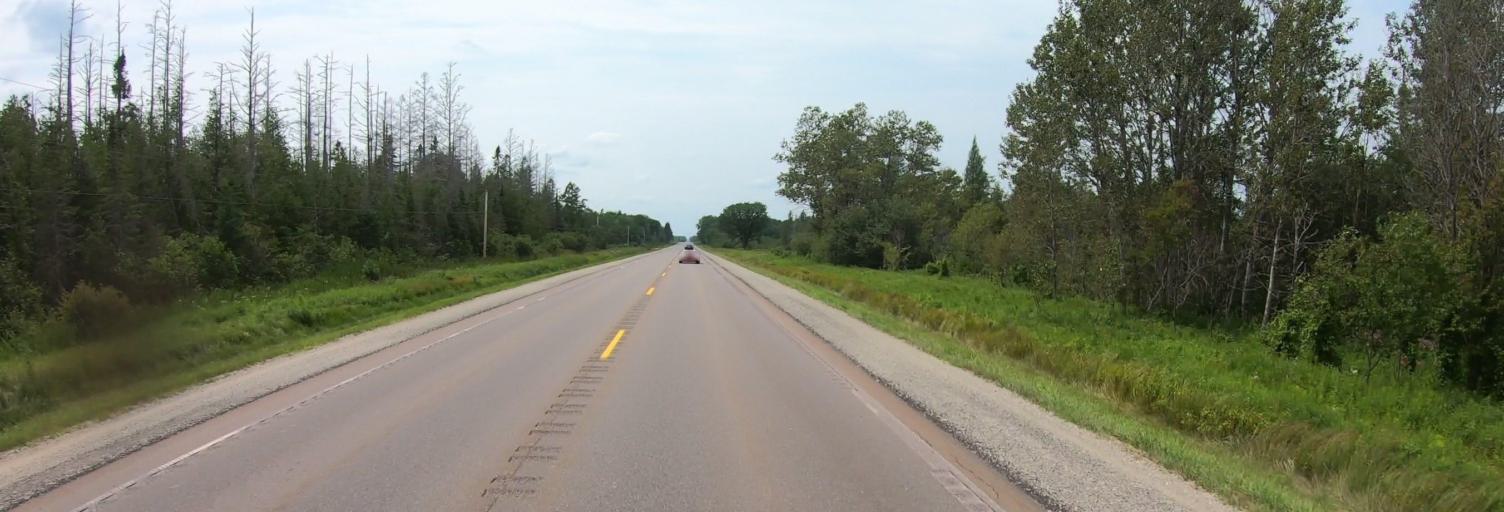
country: US
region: Michigan
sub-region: Marquette County
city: K. I. Sawyer Air Force Base
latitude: 46.3475
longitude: -87.0662
